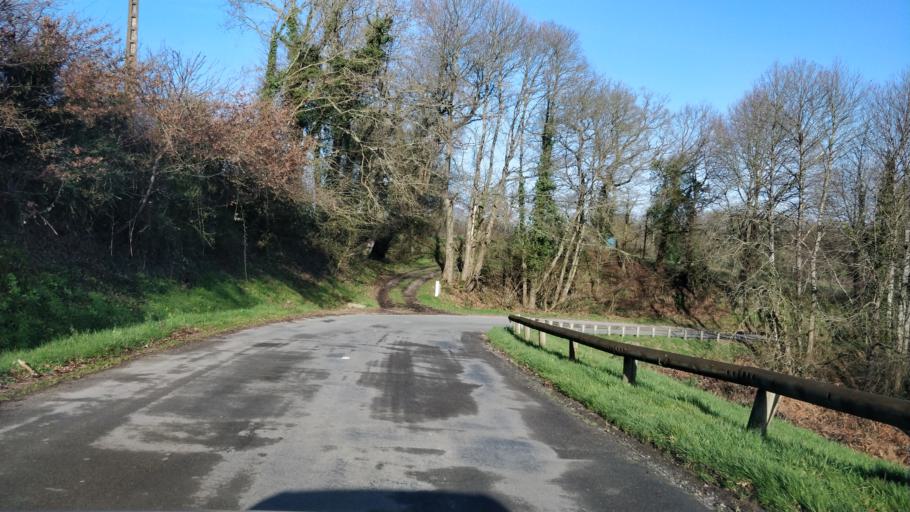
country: FR
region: Brittany
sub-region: Departement d'Ille-et-Vilaine
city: Sens-de-Bretagne
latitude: 48.3453
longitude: -1.4898
